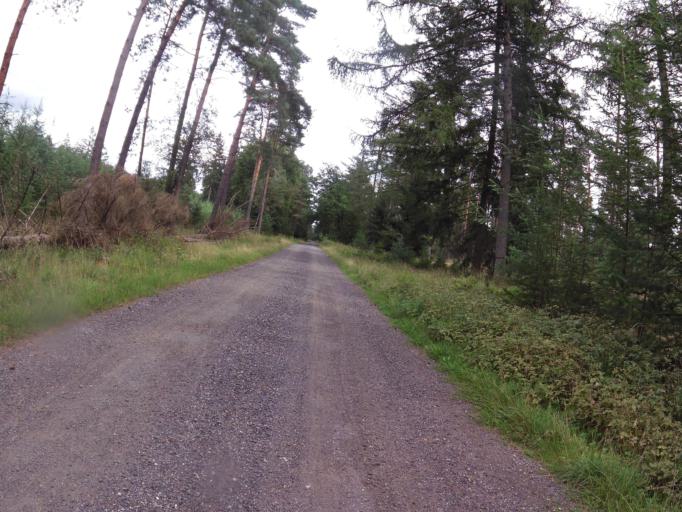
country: DE
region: Lower Saxony
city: Hipstedt
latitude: 53.5008
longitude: 8.9493
